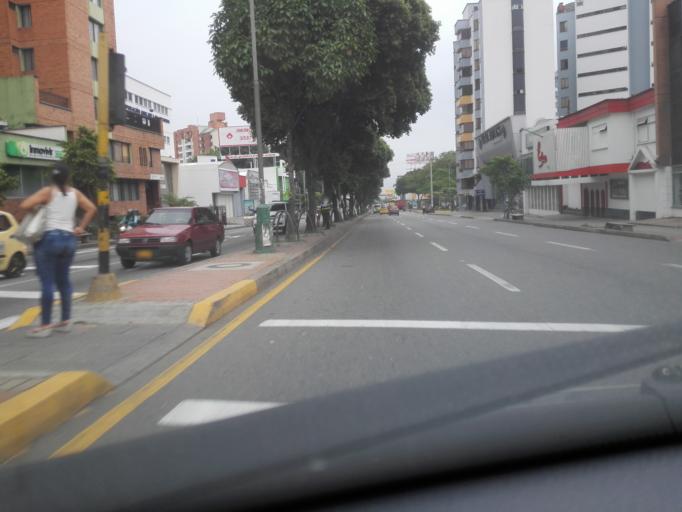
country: CO
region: Santander
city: Bucaramanga
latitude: 7.1167
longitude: -73.1153
